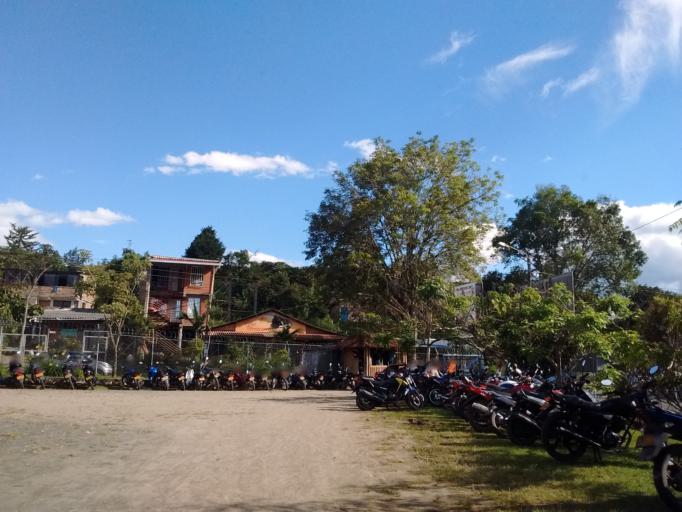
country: CO
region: Cauca
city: Popayan
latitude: 2.4760
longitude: -76.5711
